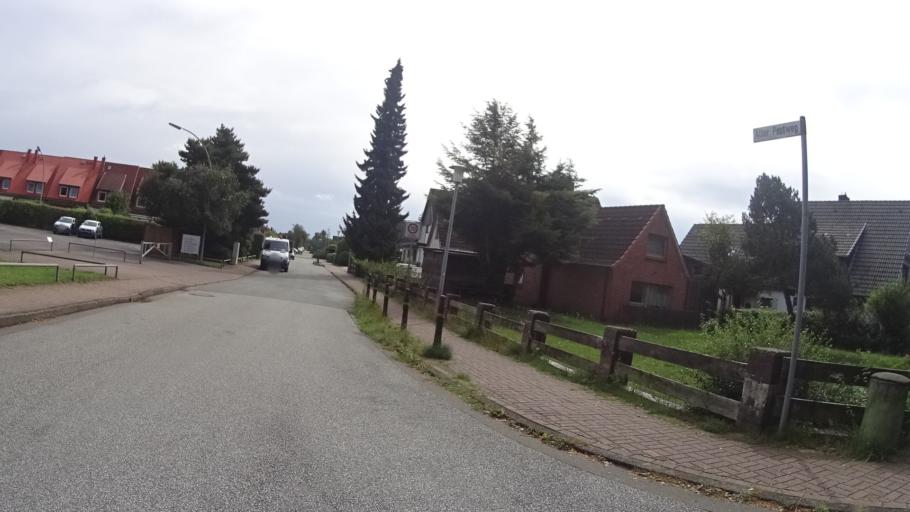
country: DE
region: Schleswig-Holstein
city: Henstedt-Ulzburg
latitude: 53.7592
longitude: 9.9970
